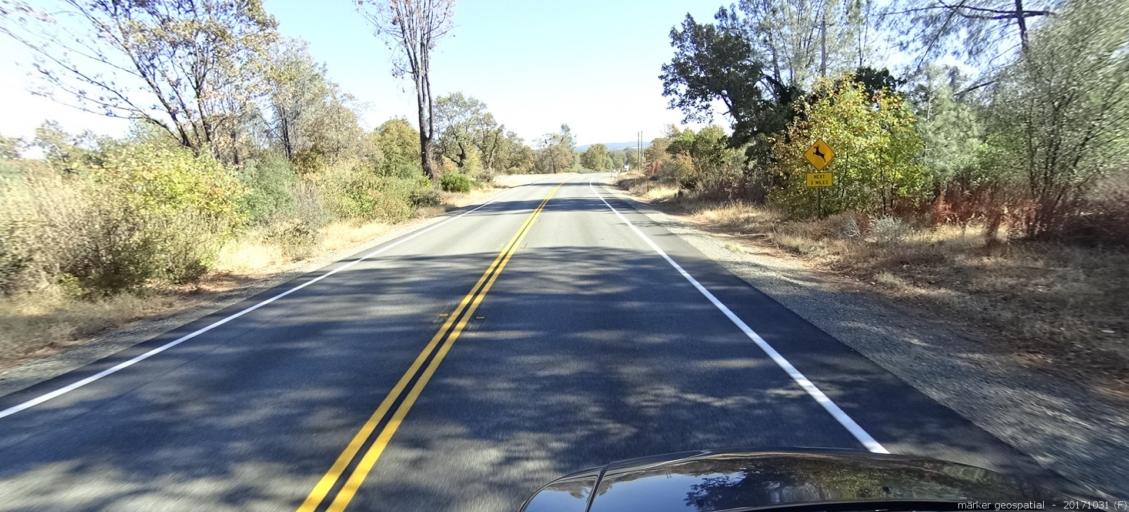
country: US
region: California
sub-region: Shasta County
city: Shingletown
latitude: 40.5138
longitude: -122.0264
